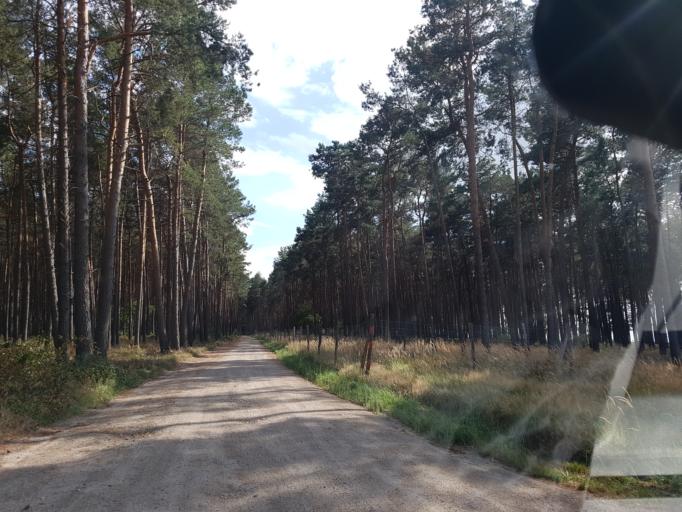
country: DE
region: Brandenburg
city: Treuenbrietzen
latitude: 52.0190
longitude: 12.8406
